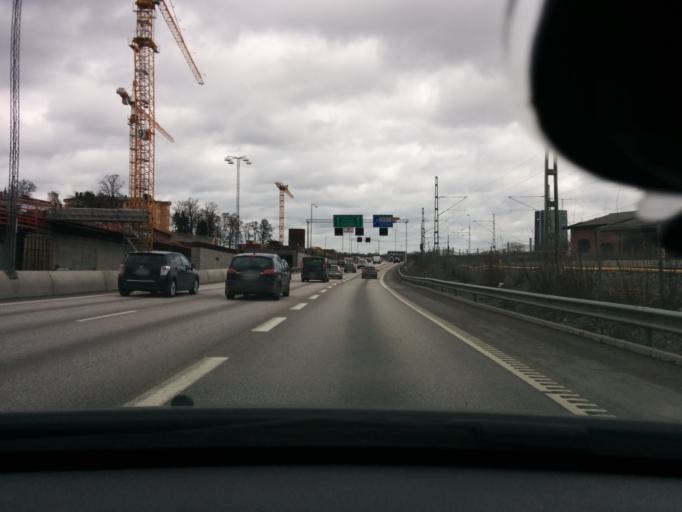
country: SE
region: Stockholm
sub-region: Norrtalje Kommun
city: Bergshamra
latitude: 59.3486
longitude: 18.0357
